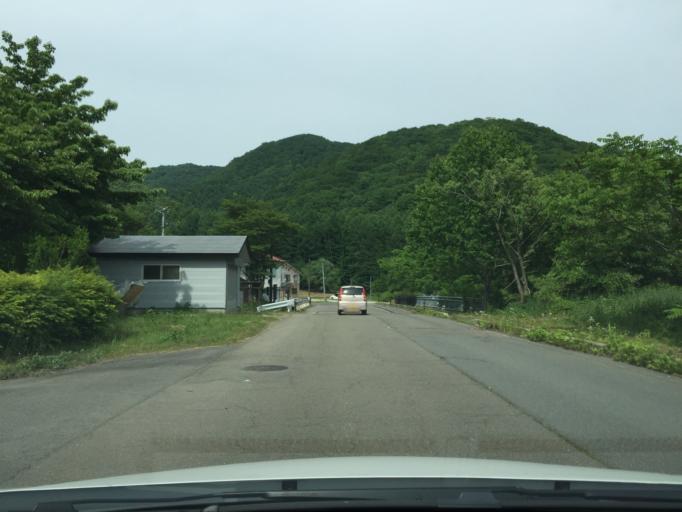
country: JP
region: Fukushima
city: Inawashiro
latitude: 37.7308
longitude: 140.0495
